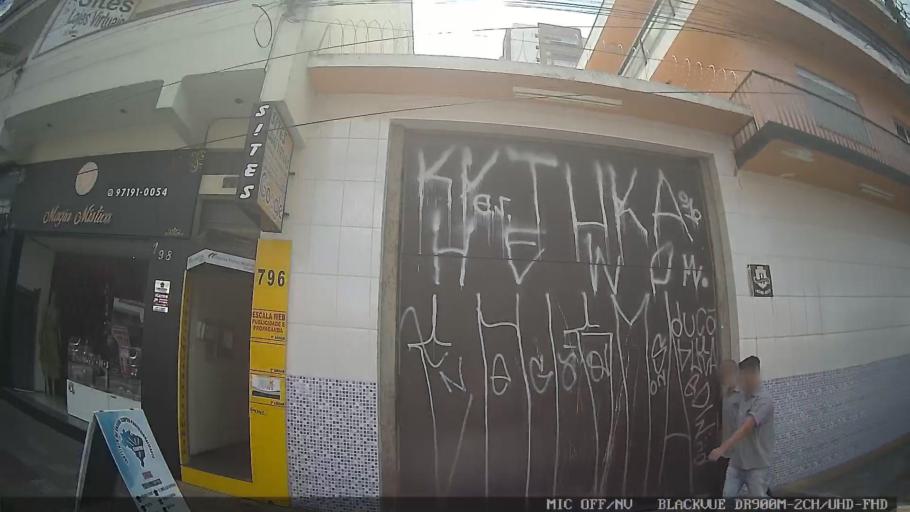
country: BR
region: Sao Paulo
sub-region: Suzano
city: Suzano
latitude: -23.5411
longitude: -46.3119
